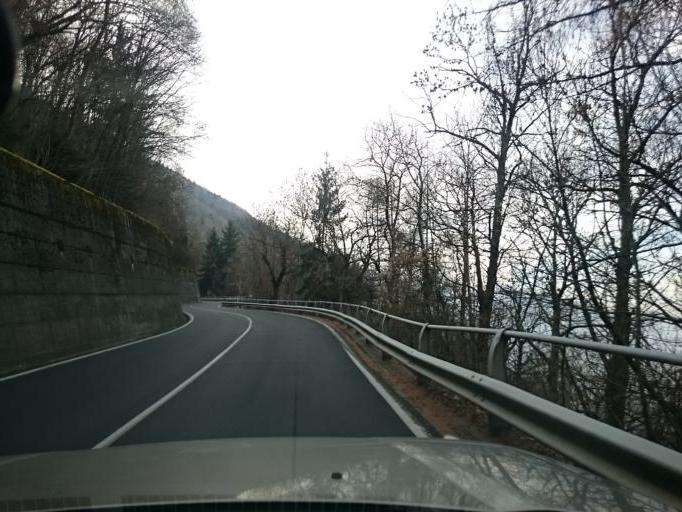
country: IT
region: Lombardy
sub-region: Provincia di Sondrio
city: Aprica
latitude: 46.1629
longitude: 10.1242
